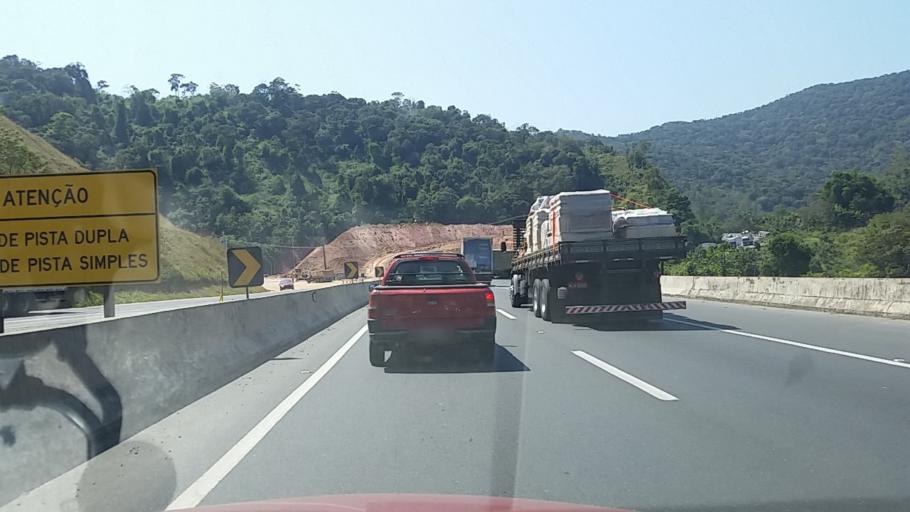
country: BR
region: Sao Paulo
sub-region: Miracatu
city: Miracatu
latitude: -24.1219
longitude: -47.2703
